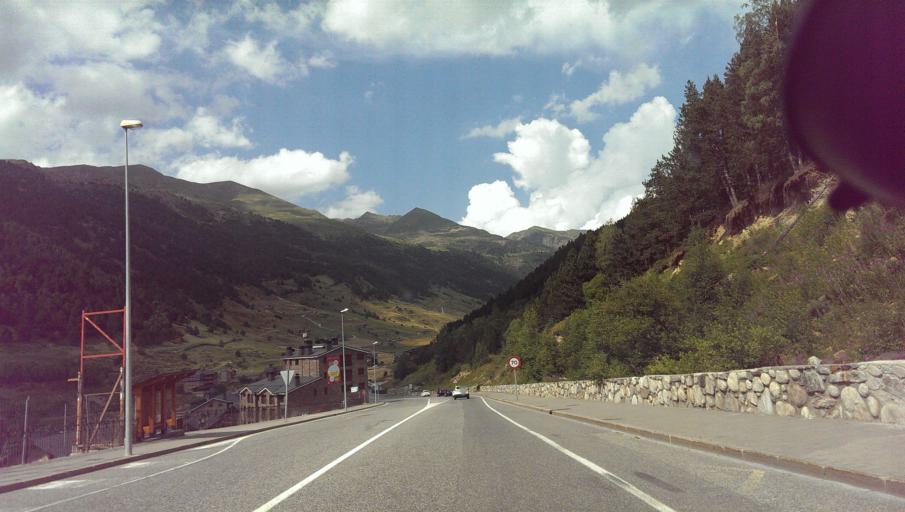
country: AD
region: Canillo
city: El Tarter
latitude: 42.5802
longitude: 1.6639
